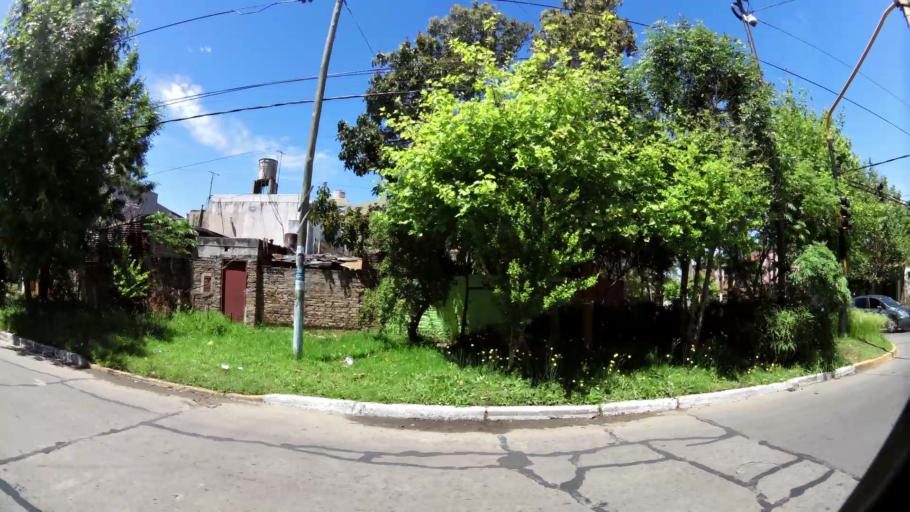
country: AR
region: Buenos Aires
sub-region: Partido de Quilmes
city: Quilmes
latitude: -34.7310
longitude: -58.2758
